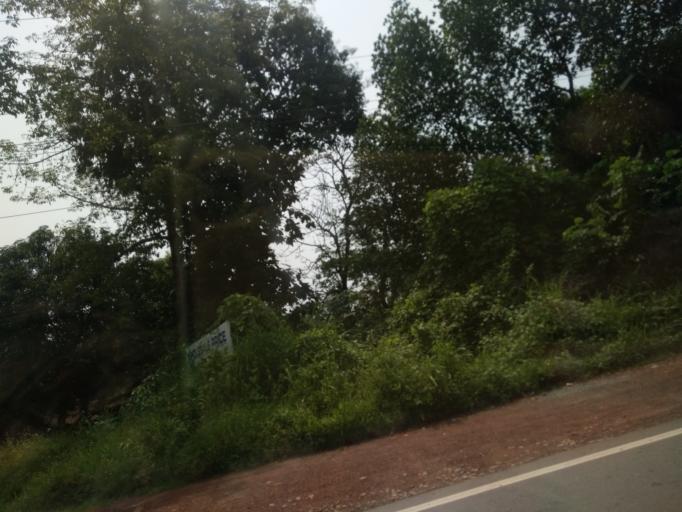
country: IN
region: Goa
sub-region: South Goa
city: Raia
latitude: 15.3299
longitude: 73.9315
